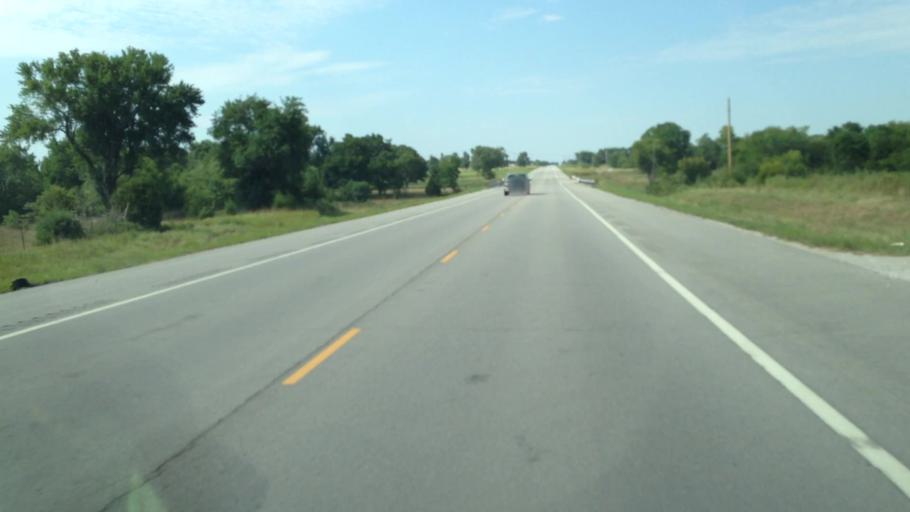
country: US
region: Kansas
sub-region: Labette County
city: Parsons
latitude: 37.2707
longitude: -95.2673
